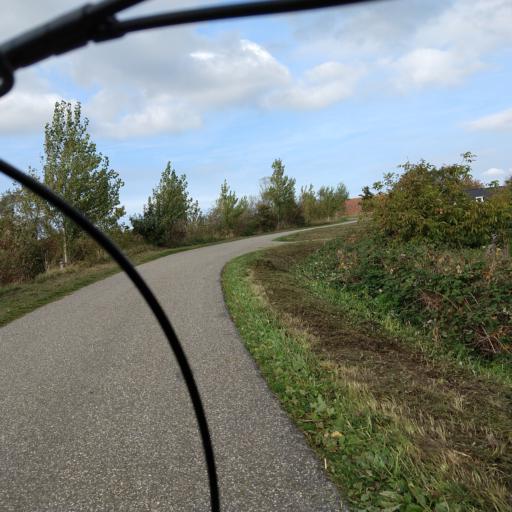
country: NL
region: Zeeland
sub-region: Schouwen-Duiveland
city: Scharendijke
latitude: 51.7014
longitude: 3.9322
